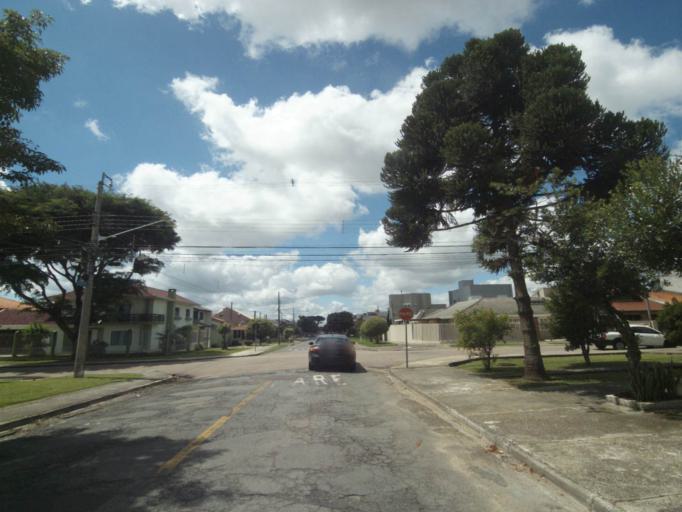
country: BR
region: Parana
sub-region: Pinhais
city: Pinhais
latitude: -25.4370
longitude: -49.2173
